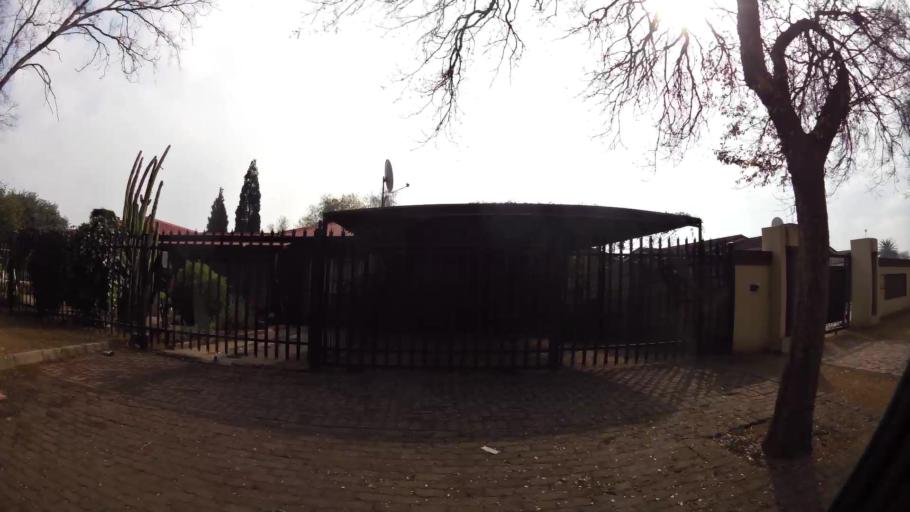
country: ZA
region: Gauteng
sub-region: Sedibeng District Municipality
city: Vanderbijlpark
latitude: -26.6908
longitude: 27.8392
